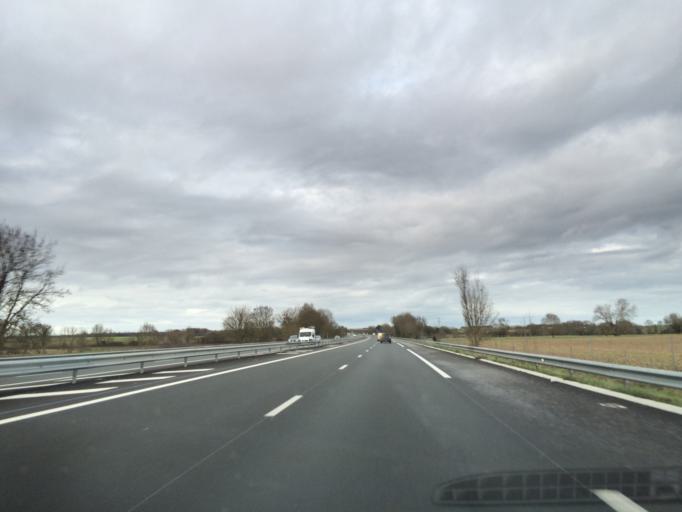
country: FR
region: Poitou-Charentes
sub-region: Departement des Deux-Sevres
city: Beauvoir-sur-Niort
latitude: 46.1519
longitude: -0.5193
